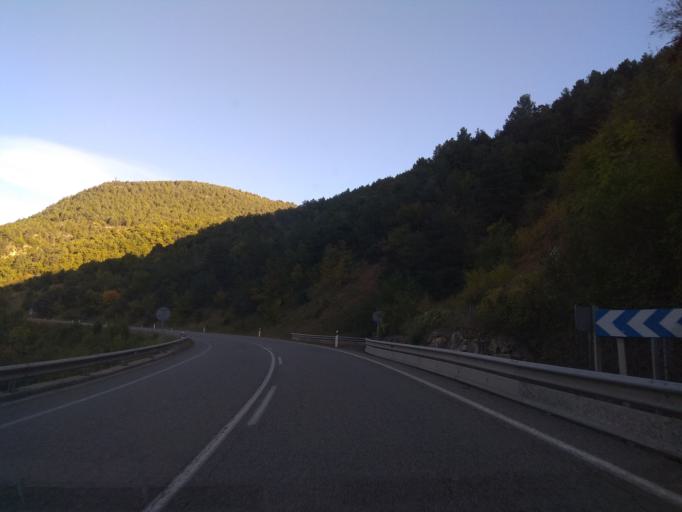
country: ES
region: Catalonia
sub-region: Provincia de Lleida
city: el Pont de Bar
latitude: 42.3692
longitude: 1.6108
